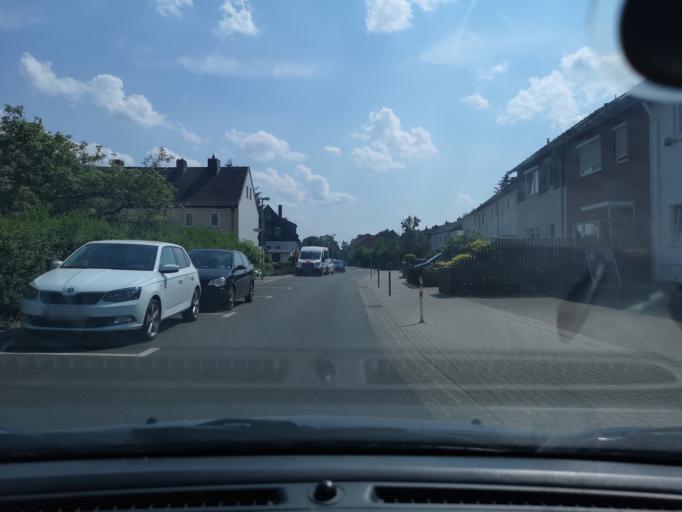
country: DE
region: Lower Saxony
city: Langenhagen
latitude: 52.4345
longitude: 9.7381
